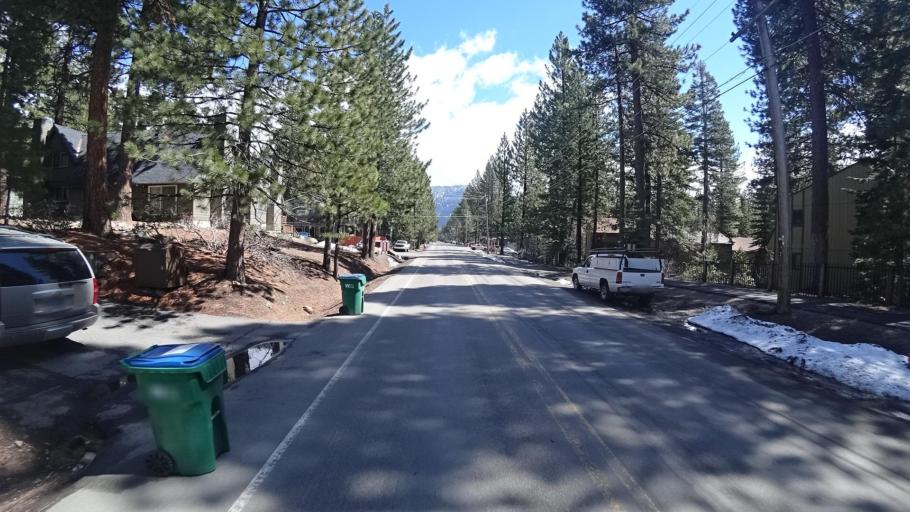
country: US
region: Nevada
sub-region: Washoe County
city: Incline Village
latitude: 39.2474
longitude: -119.9597
